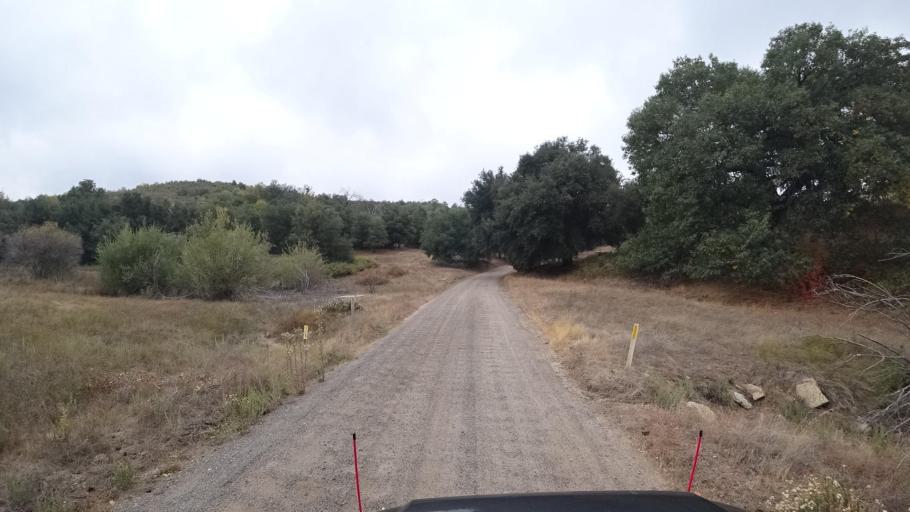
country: US
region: California
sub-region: San Diego County
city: Julian
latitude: 33.0043
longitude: -116.6373
